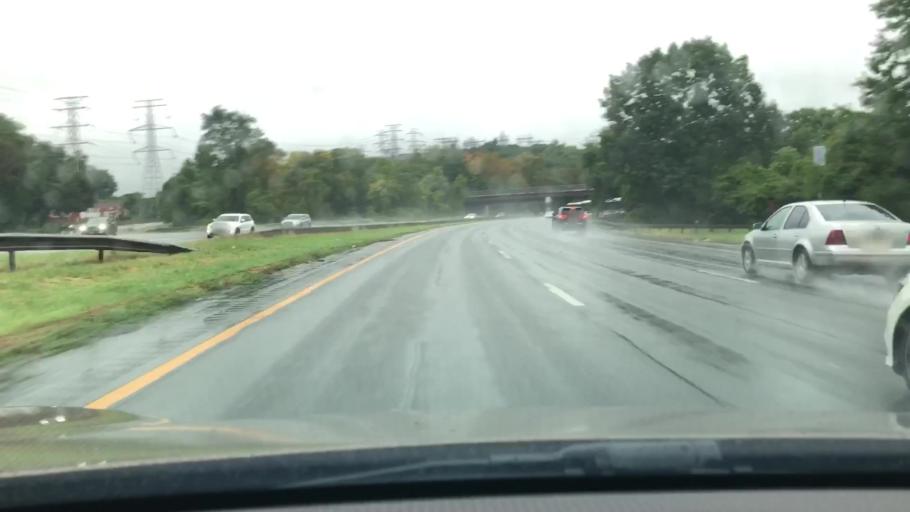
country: US
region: New York
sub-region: Westchester County
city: Bronxville
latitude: 40.9504
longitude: -73.8527
